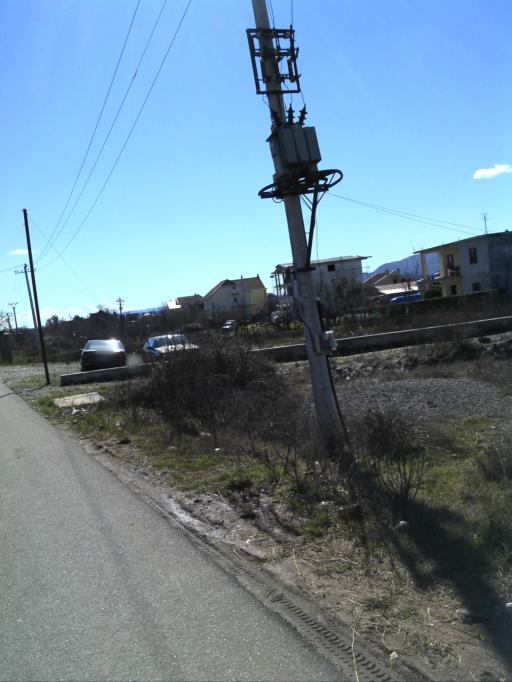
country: AL
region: Shkoder
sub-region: Rrethi i Shkodres
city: Shkoder
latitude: 42.1078
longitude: 19.5026
